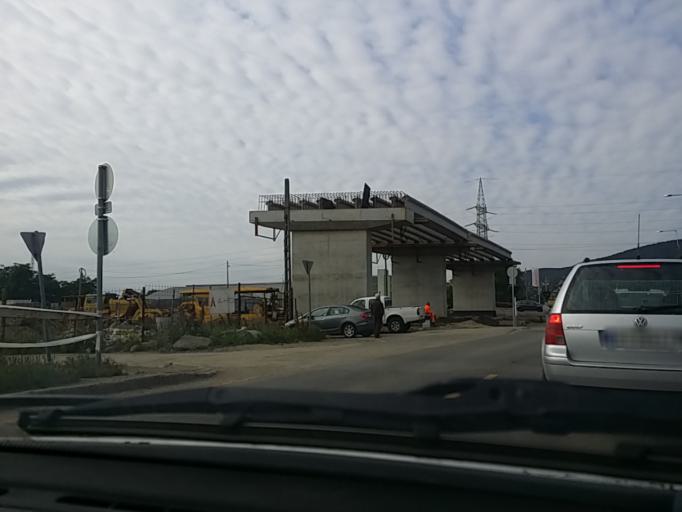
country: HU
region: Pest
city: Urom
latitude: 47.5707
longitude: 19.0291
